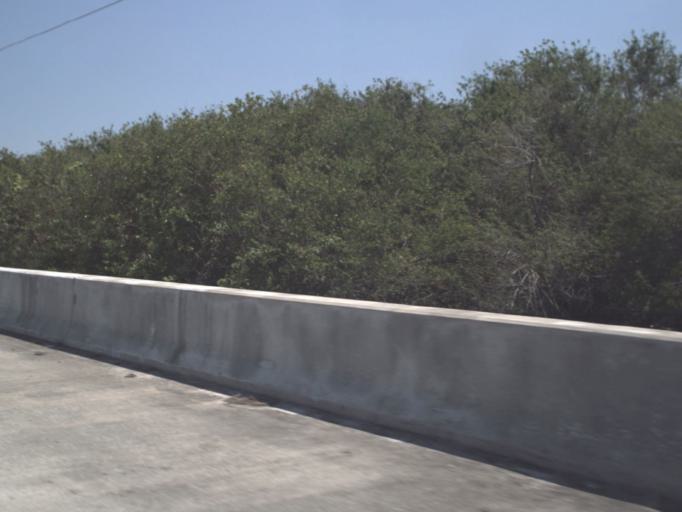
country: US
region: Florida
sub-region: Brevard County
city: Grant-Valkaria
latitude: 27.9684
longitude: -80.5445
